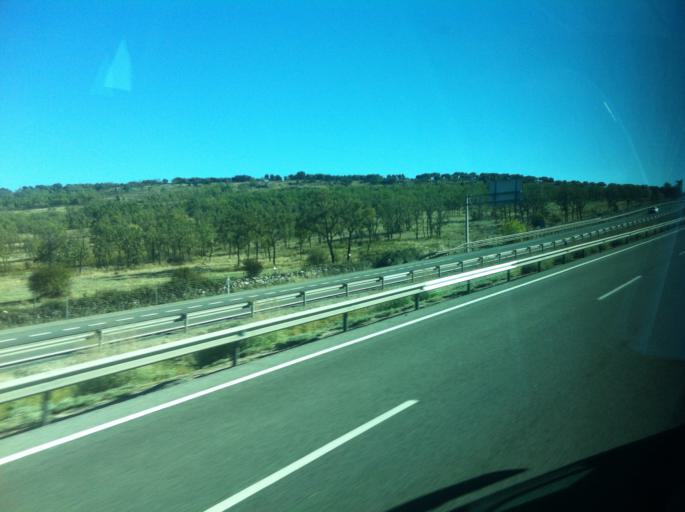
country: ES
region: Madrid
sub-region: Provincia de Madrid
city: Buitrago del Lozoya
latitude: 40.9633
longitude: -3.6417
